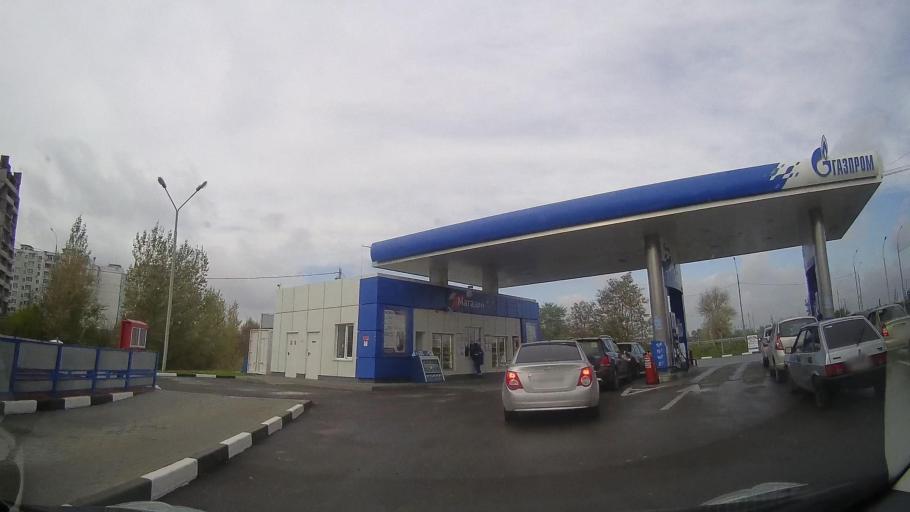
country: RU
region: Rostov
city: Bataysk
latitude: 47.1574
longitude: 39.7449
